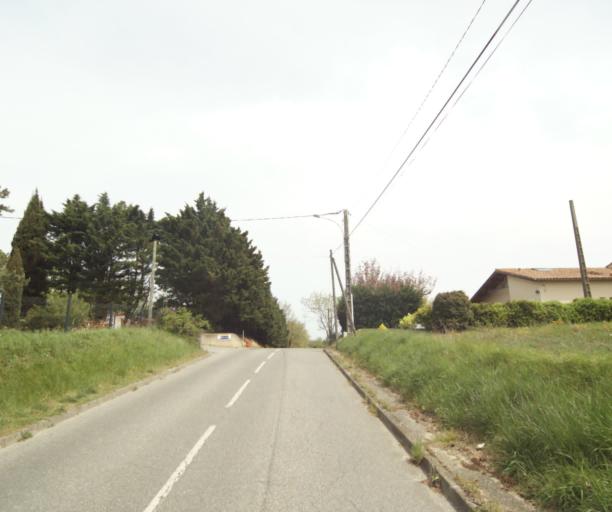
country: FR
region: Midi-Pyrenees
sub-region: Departement de la Haute-Garonne
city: Castanet-Tolosan
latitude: 43.5079
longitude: 1.4879
